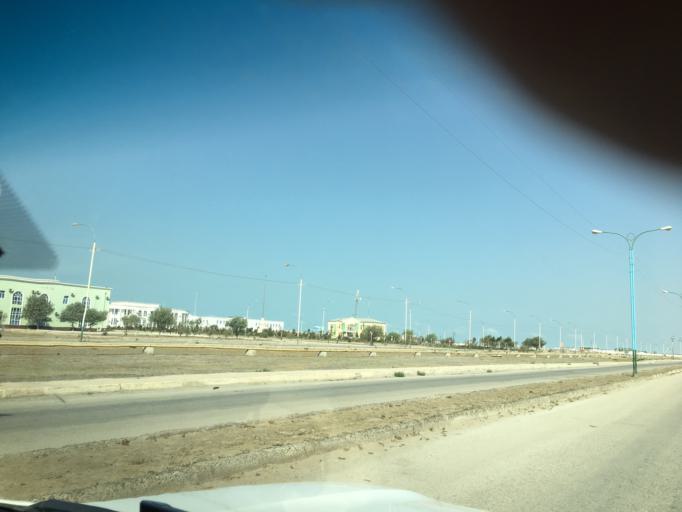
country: IR
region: Golestan
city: Gomishan
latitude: 37.4774
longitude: 53.9778
